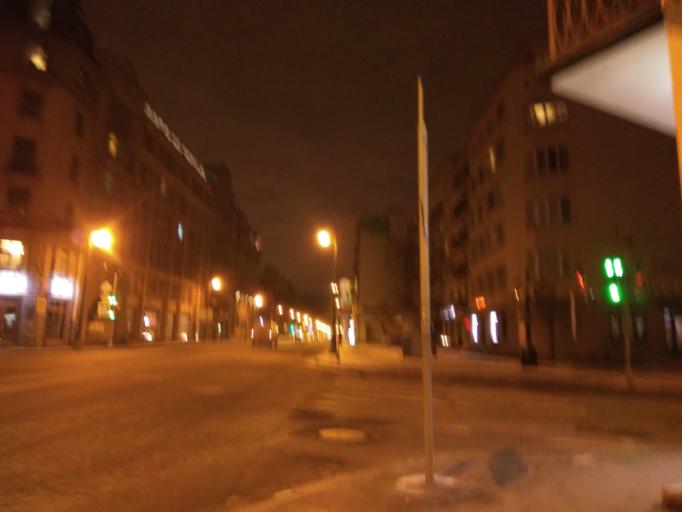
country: RU
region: St.-Petersburg
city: Petrogradka
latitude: 59.9710
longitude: 30.3068
